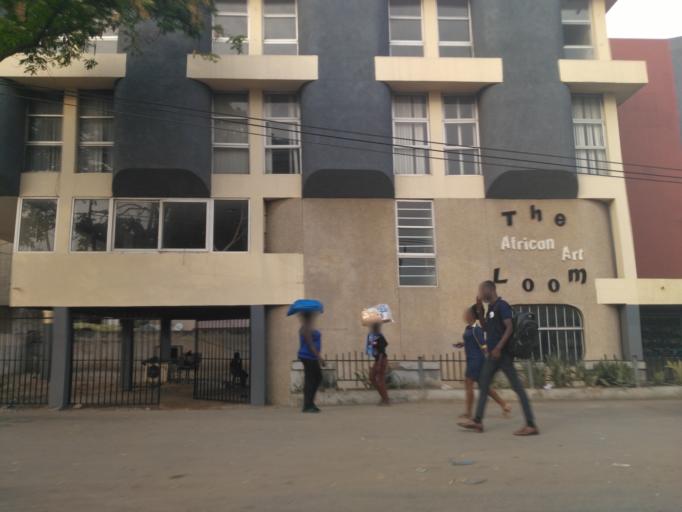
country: GH
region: Greater Accra
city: Accra
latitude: 5.5681
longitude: -0.2151
